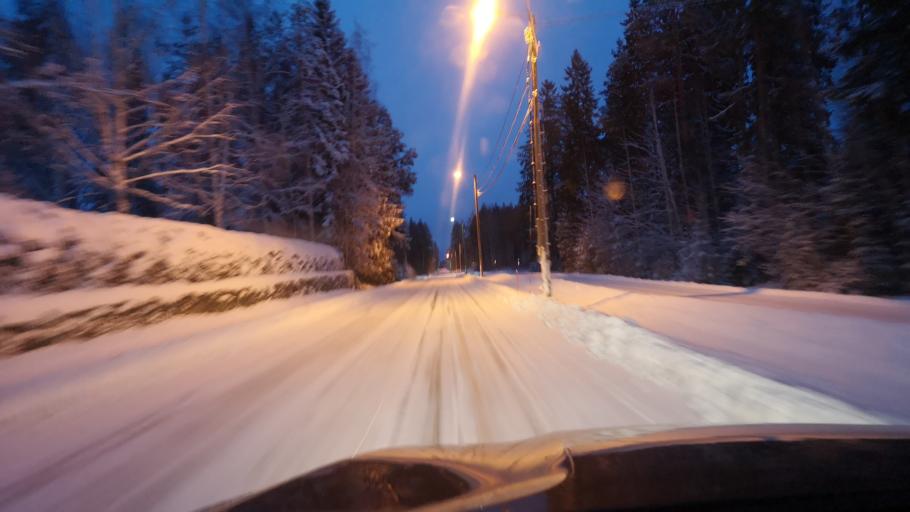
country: FI
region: Varsinais-Suomi
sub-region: Loimaa
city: Loimaa
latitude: 60.8647
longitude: 23.0829
